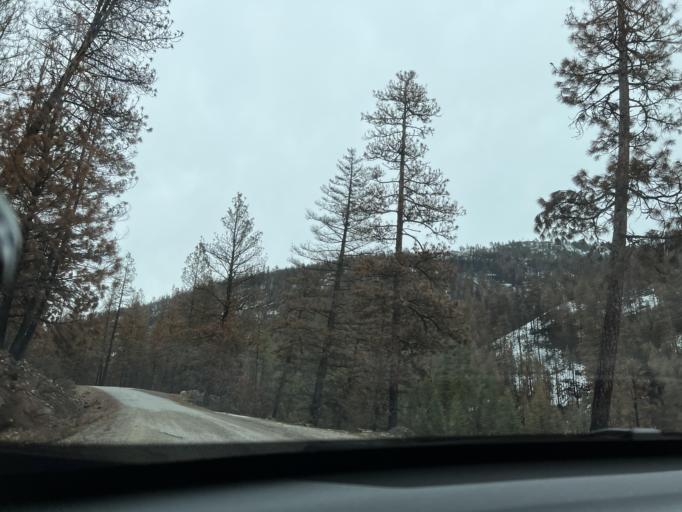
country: US
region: Washington
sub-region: Okanogan County
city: Brewster
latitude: 48.5792
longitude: -120.1577
